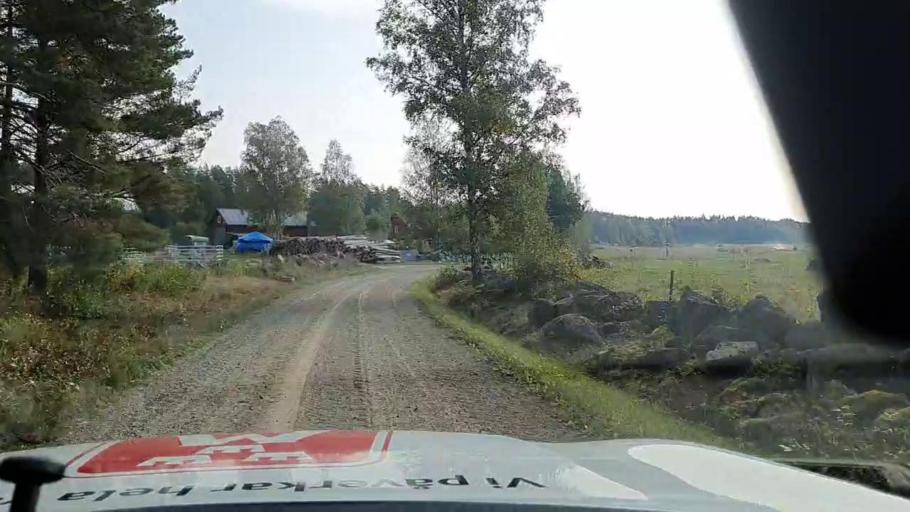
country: SE
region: Vaestmanland
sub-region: Kungsors Kommun
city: Kungsoer
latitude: 59.3559
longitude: 16.1565
